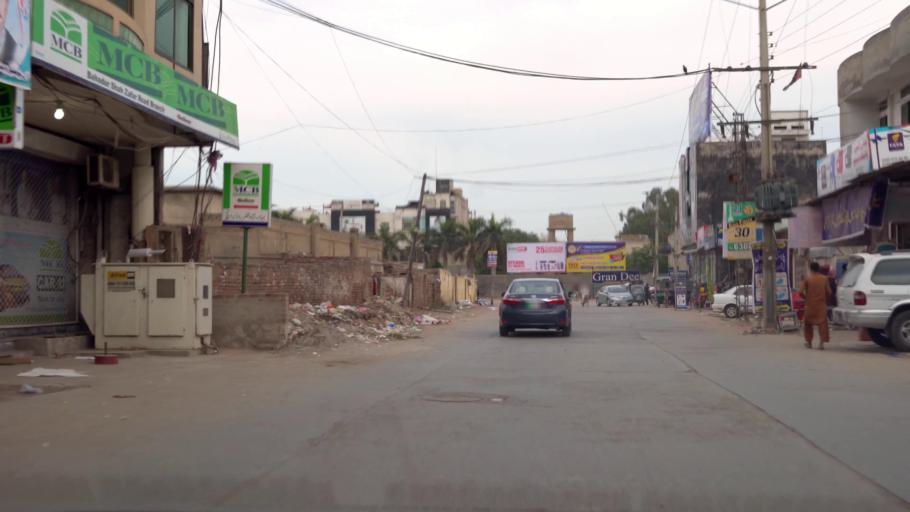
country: PK
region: Punjab
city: Sargodha
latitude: 32.0796
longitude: 72.6810
